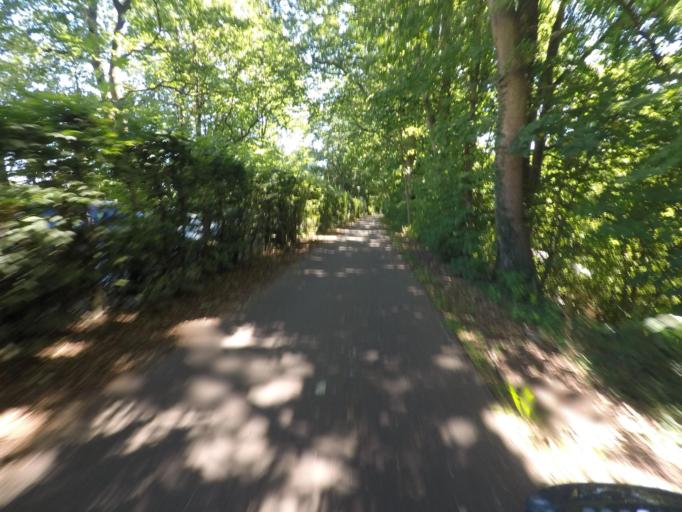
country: DE
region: Schleswig-Holstein
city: Lutjensee
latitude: 53.6445
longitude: 10.3642
